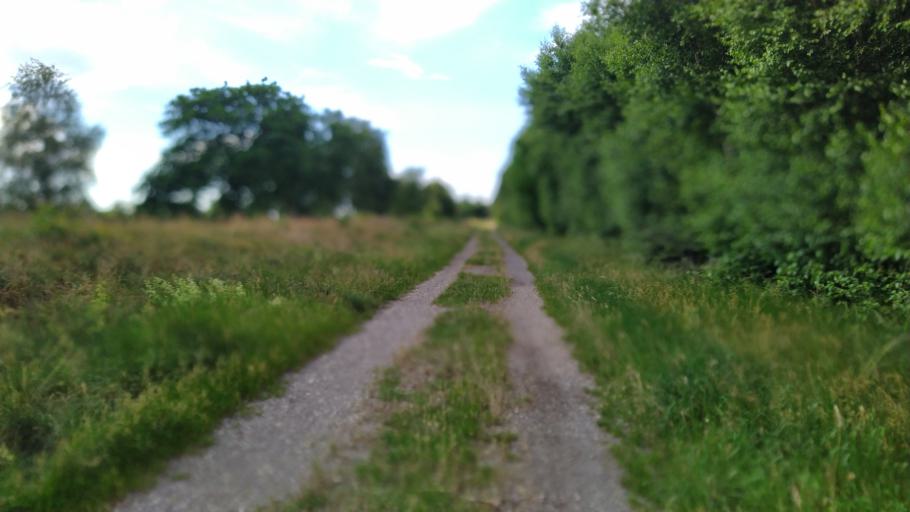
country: DE
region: Lower Saxony
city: Stinstedt
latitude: 53.6478
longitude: 8.9478
